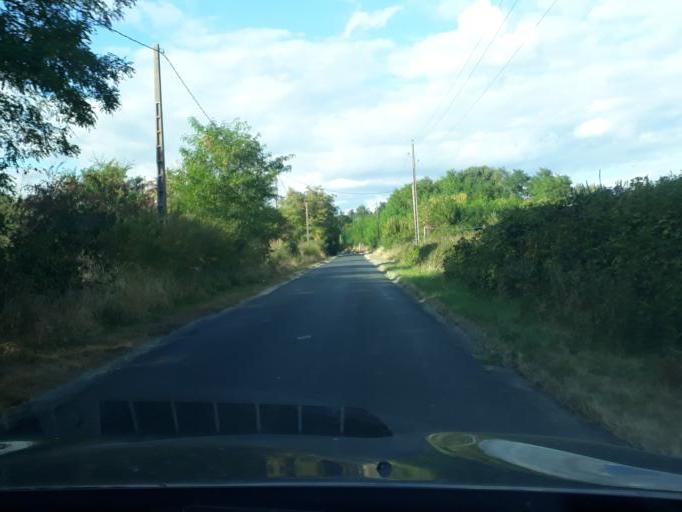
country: FR
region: Centre
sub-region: Departement du Loiret
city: Rebrechien
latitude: 47.9918
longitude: 2.0539
